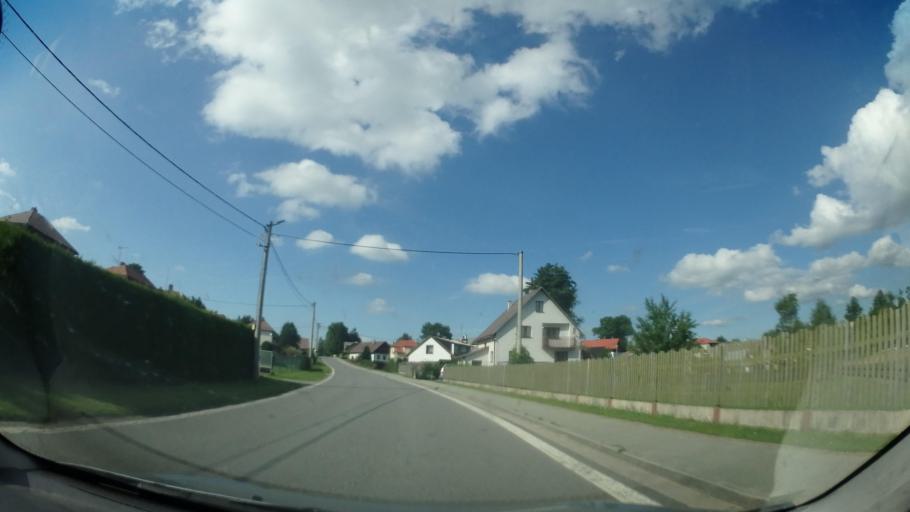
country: CZ
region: Vysocina
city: Heralec
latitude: 49.6922
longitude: 15.9928
